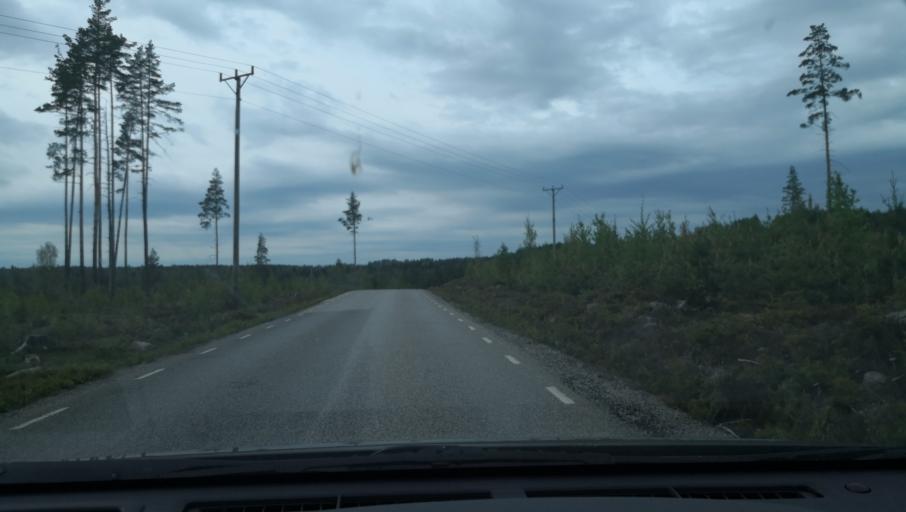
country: SE
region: Vaestmanland
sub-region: Skinnskattebergs Kommun
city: Skinnskatteberg
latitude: 59.8287
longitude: 15.5778
